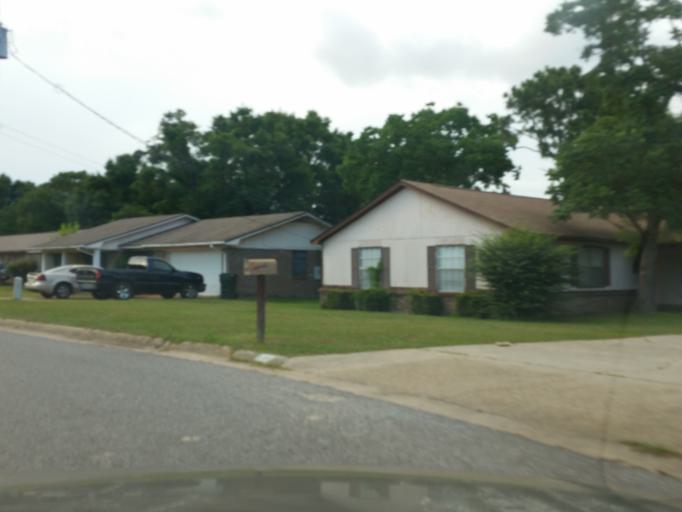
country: US
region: Florida
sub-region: Escambia County
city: Ferry Pass
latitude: 30.5119
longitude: -87.1760
